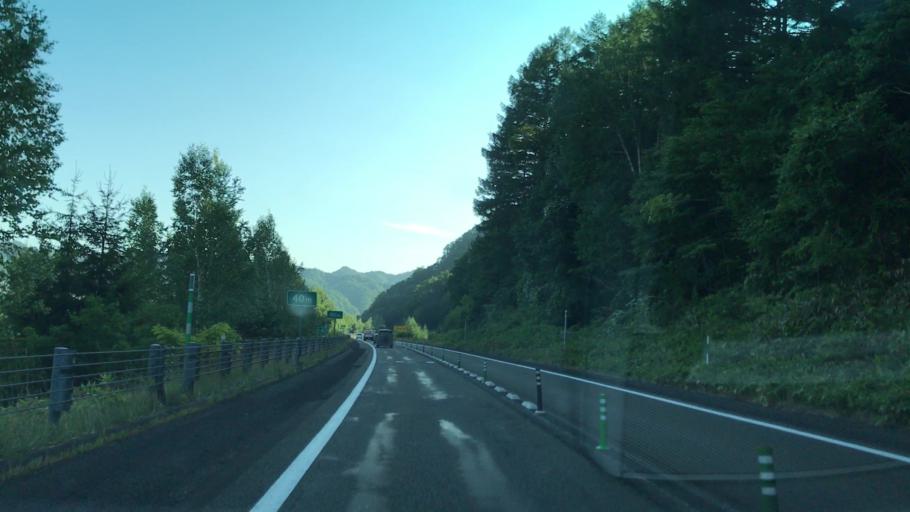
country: JP
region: Hokkaido
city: Chitose
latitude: 42.9129
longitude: 142.0185
